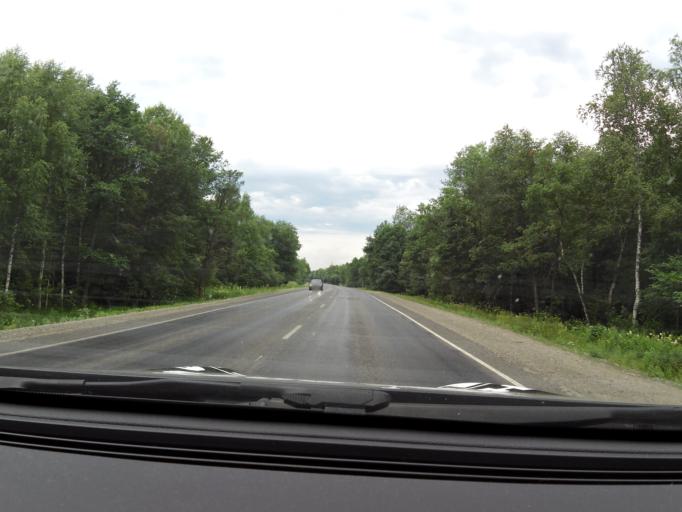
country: RU
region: Bashkortostan
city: Urman
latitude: 54.8311
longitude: 56.9401
